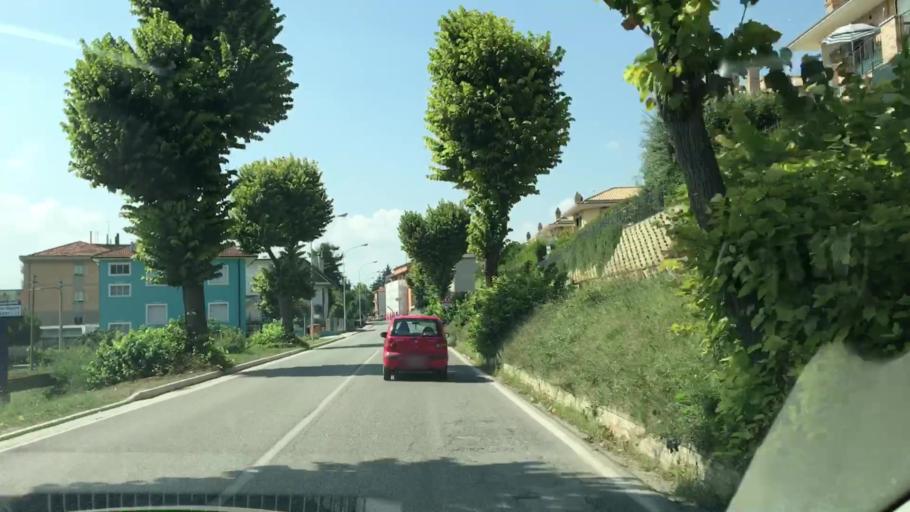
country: IT
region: The Marches
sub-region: Provincia di Ascoli Piceno
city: Stella
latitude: 42.8891
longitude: 13.8220
